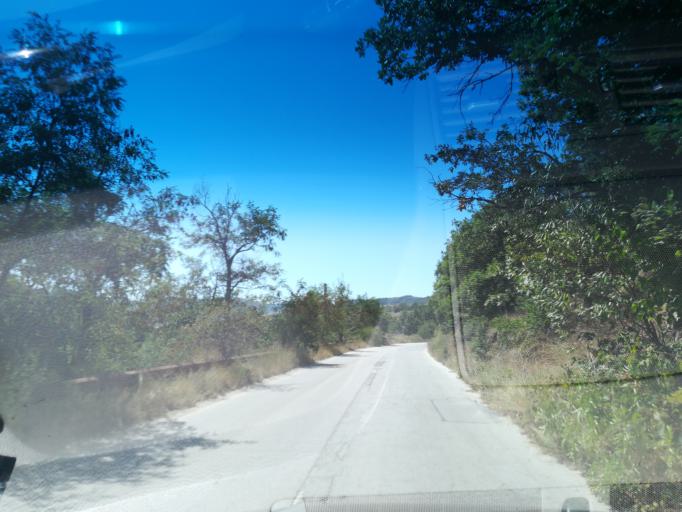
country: BG
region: Pazardzhik
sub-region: Obshtina Strelcha
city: Strelcha
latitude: 42.5245
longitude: 24.3250
